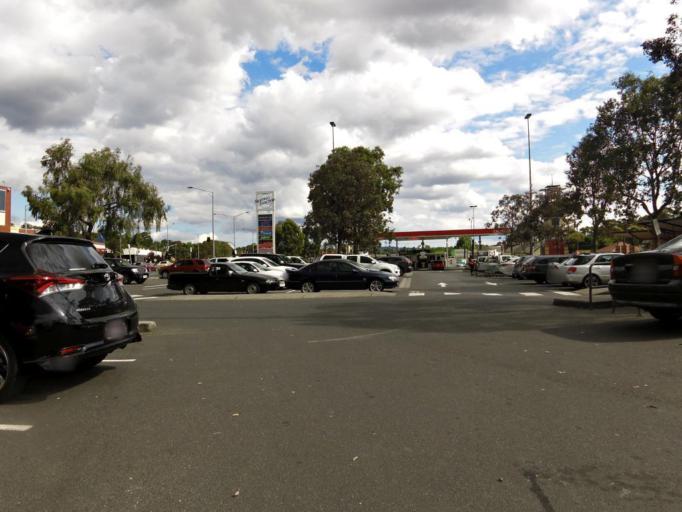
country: AU
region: Victoria
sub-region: Knox
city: Boronia
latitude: -37.8615
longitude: 145.2852
